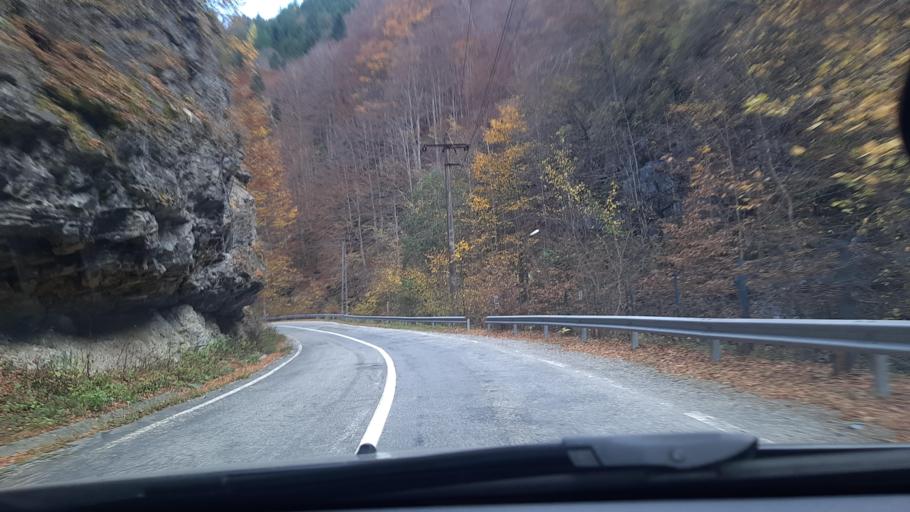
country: RO
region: Valcea
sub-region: Comuna Voineasa
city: Voineasa
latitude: 45.4259
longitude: 23.9116
